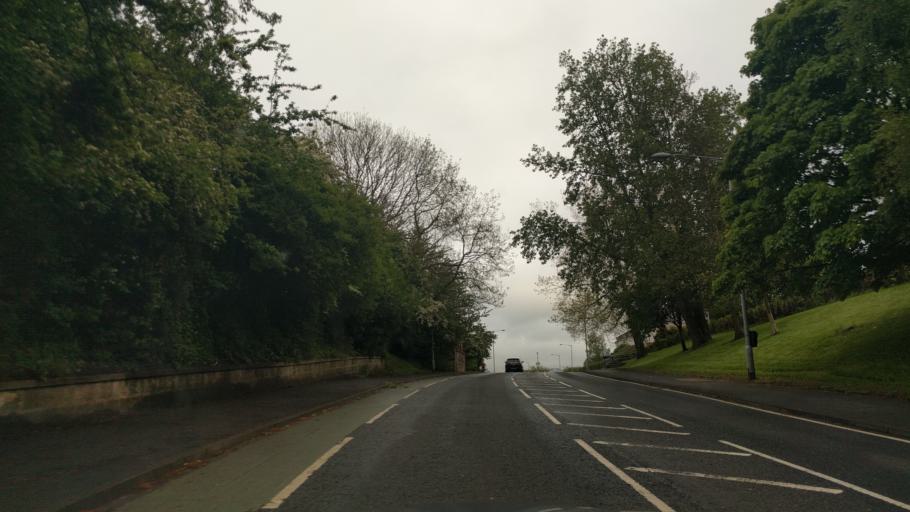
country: GB
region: England
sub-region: Northumberland
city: Morpeth
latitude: 55.1613
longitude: -1.6827
